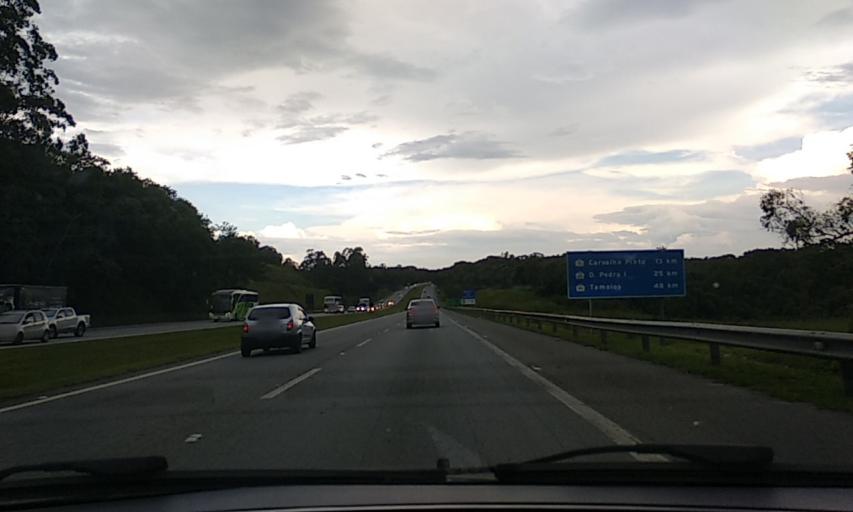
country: BR
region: Sao Paulo
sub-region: Aruja
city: Aruja
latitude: -23.4360
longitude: -46.2395
